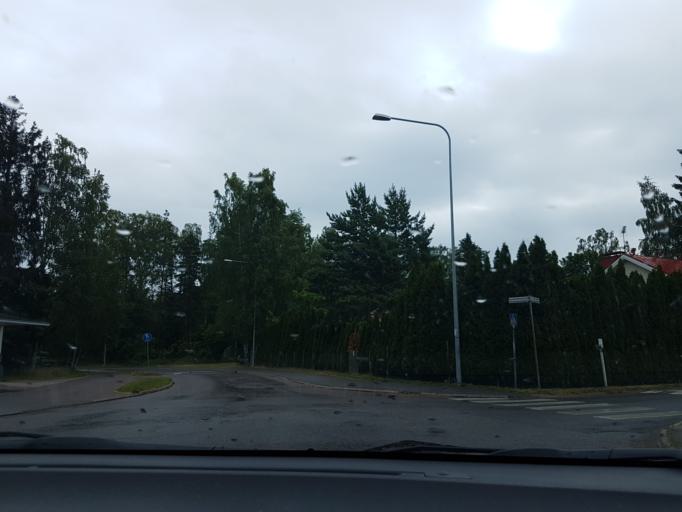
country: FI
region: Uusimaa
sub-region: Helsinki
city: Vantaa
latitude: 60.2425
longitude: 25.0939
